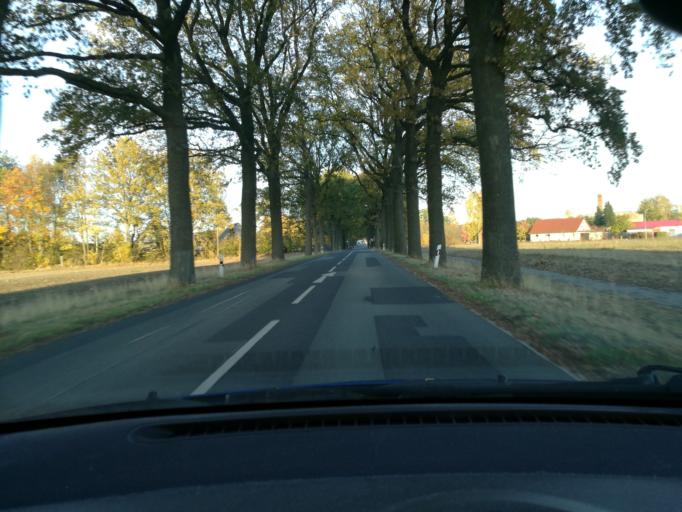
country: DE
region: Brandenburg
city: Perleberg
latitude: 53.0834
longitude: 11.8887
